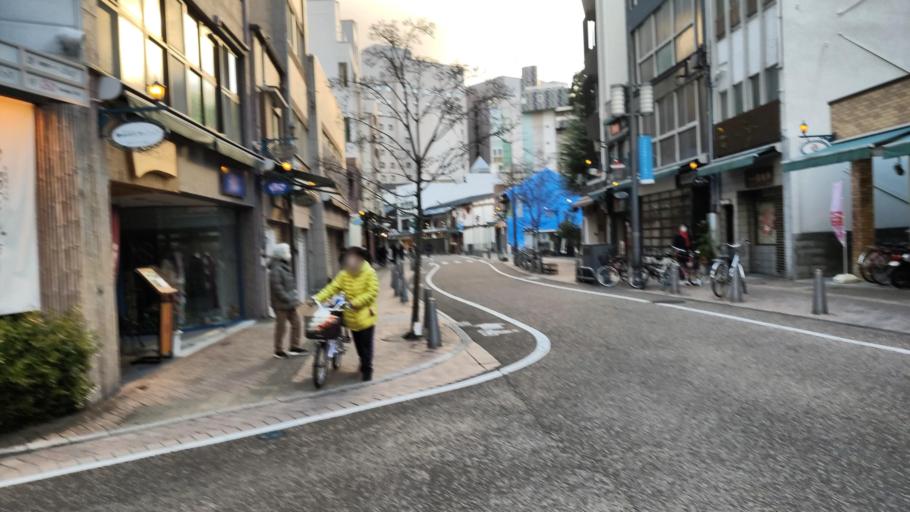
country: JP
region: Ehime
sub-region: Shikoku-chuo Shi
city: Matsuyama
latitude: 33.8427
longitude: 132.7708
